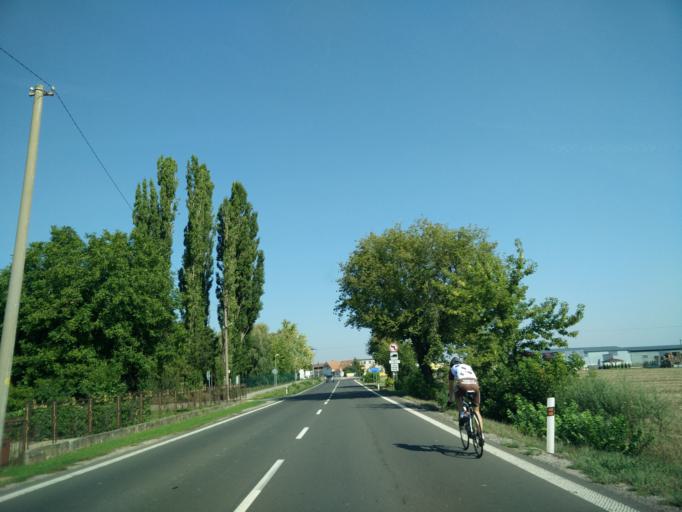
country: SK
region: Nitriansky
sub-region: Okres Nitra
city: Nitra
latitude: 48.3715
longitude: 18.0416
